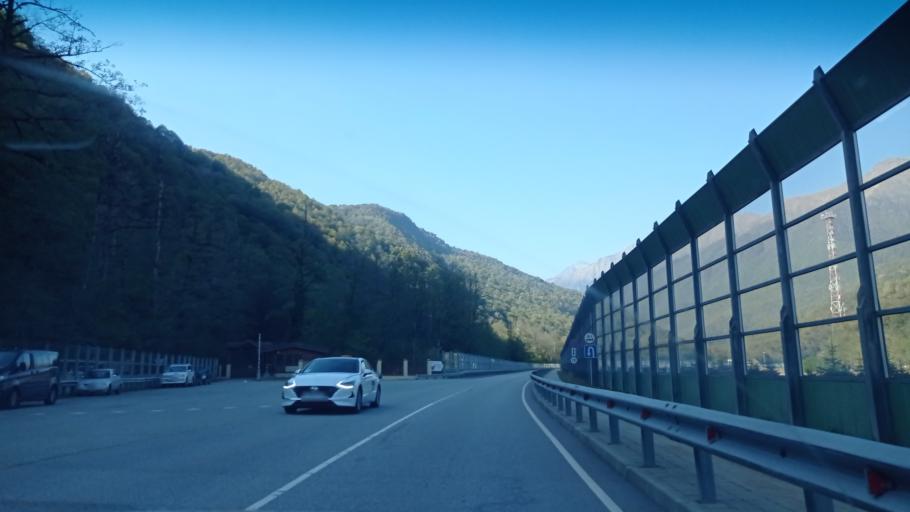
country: RU
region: Krasnodarskiy
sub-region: Sochi City
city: Krasnaya Polyana
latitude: 43.6913
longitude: 40.2717
